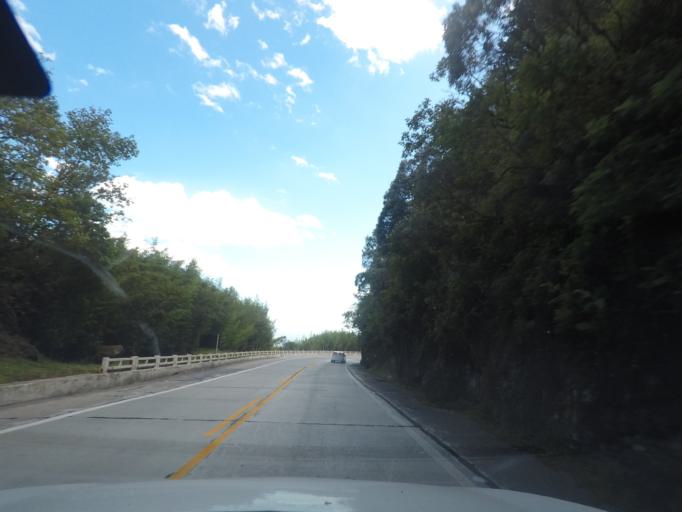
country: BR
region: Rio de Janeiro
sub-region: Guapimirim
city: Guapimirim
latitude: -22.4793
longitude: -42.9975
